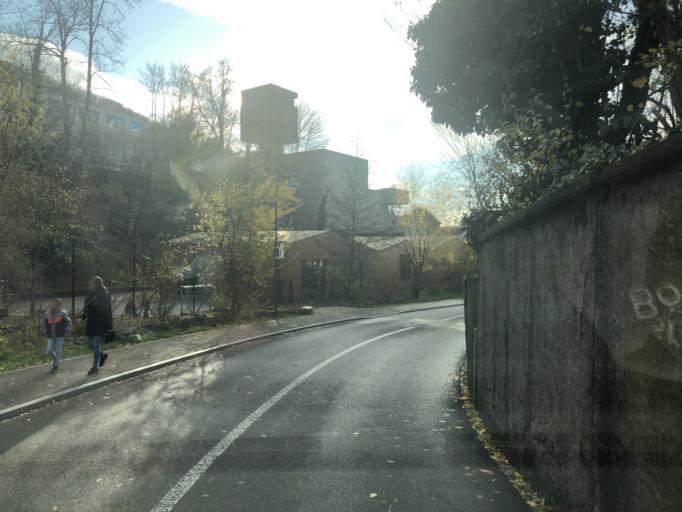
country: CH
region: Aargau
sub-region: Bezirk Baden
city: Wettingen
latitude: 47.4797
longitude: 8.3187
